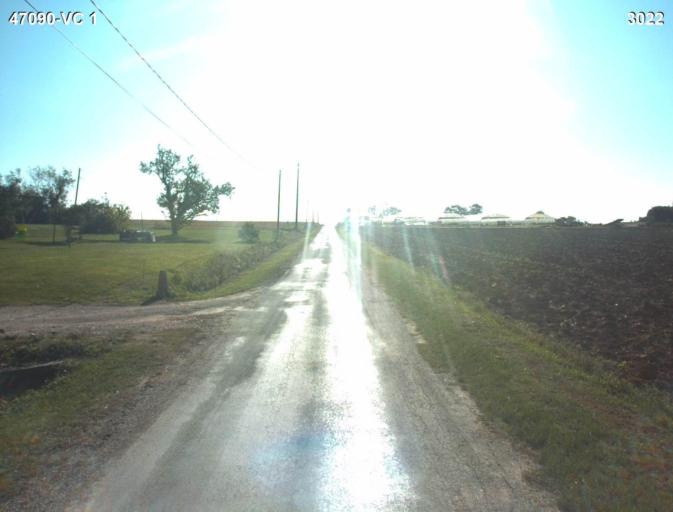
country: FR
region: Aquitaine
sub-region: Departement du Lot-et-Garonne
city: Nerac
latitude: 44.1524
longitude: 0.3980
